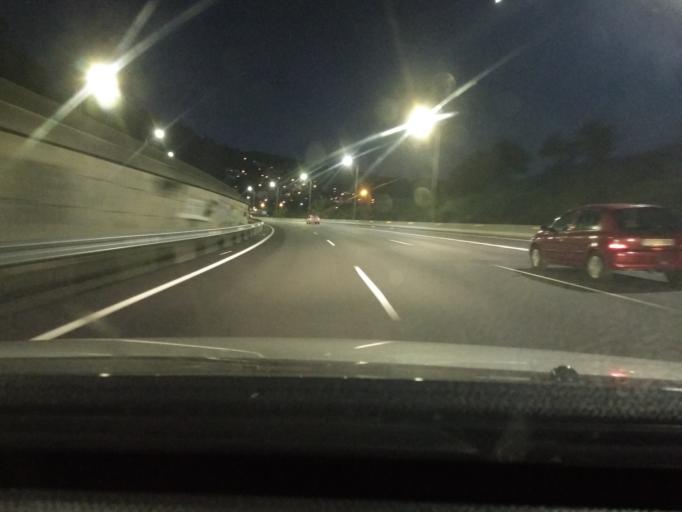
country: ES
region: Galicia
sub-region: Provincia de Pontevedra
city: Redondela
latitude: 42.2747
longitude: -8.6661
